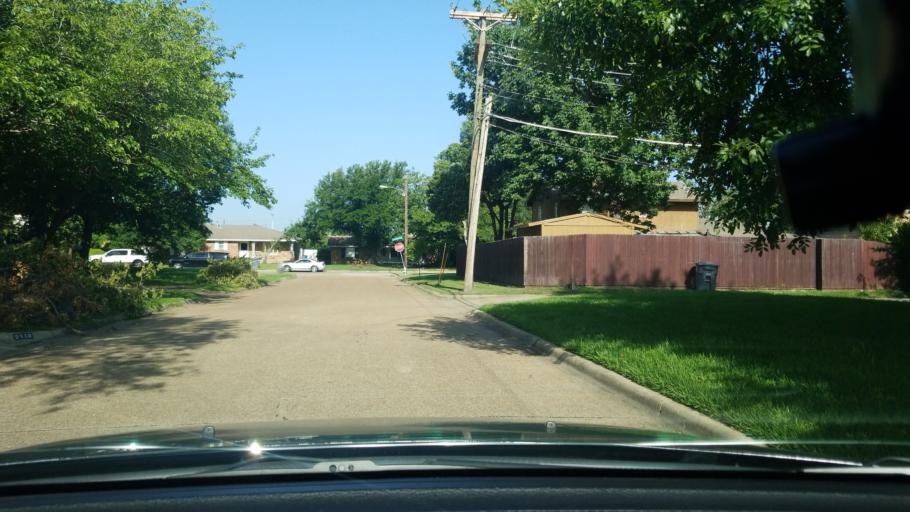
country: US
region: Texas
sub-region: Dallas County
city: Mesquite
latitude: 32.8076
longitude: -96.6795
